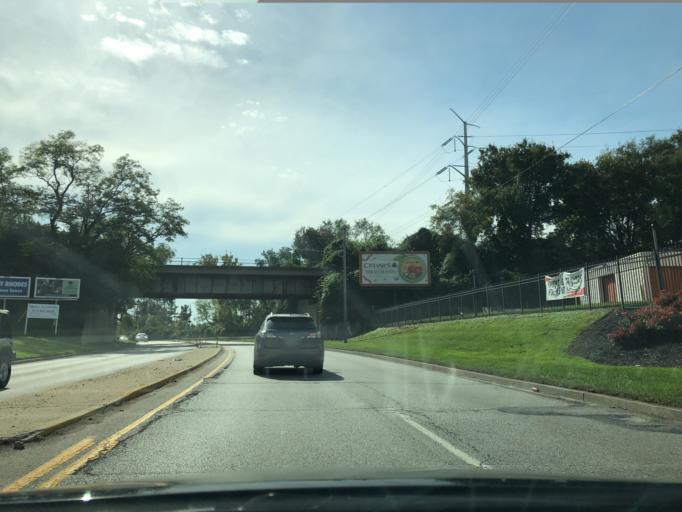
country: US
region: Ohio
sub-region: Hamilton County
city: Fairfax
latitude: 39.1574
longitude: -84.4063
